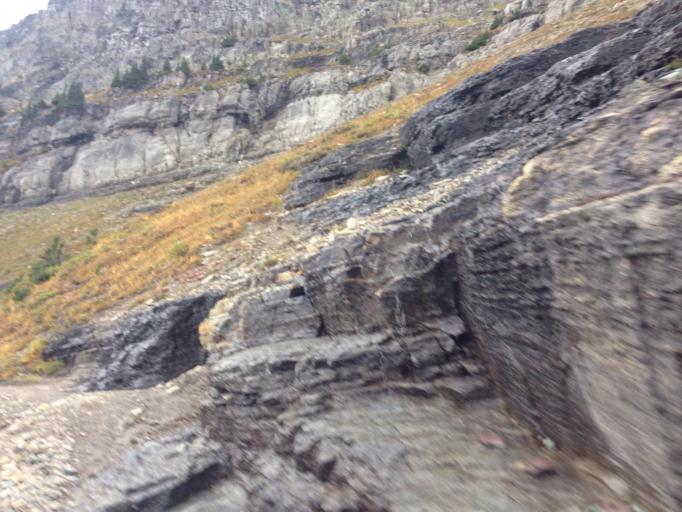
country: US
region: Montana
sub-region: Flathead County
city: Columbia Falls
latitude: 48.7427
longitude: -113.7295
